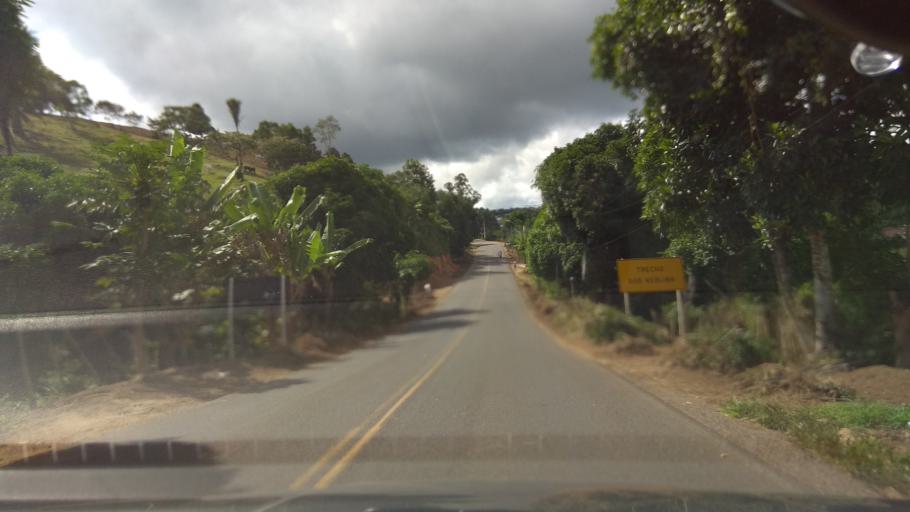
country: BR
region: Bahia
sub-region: Mutuipe
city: Mutuipe
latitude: -13.2550
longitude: -39.5788
